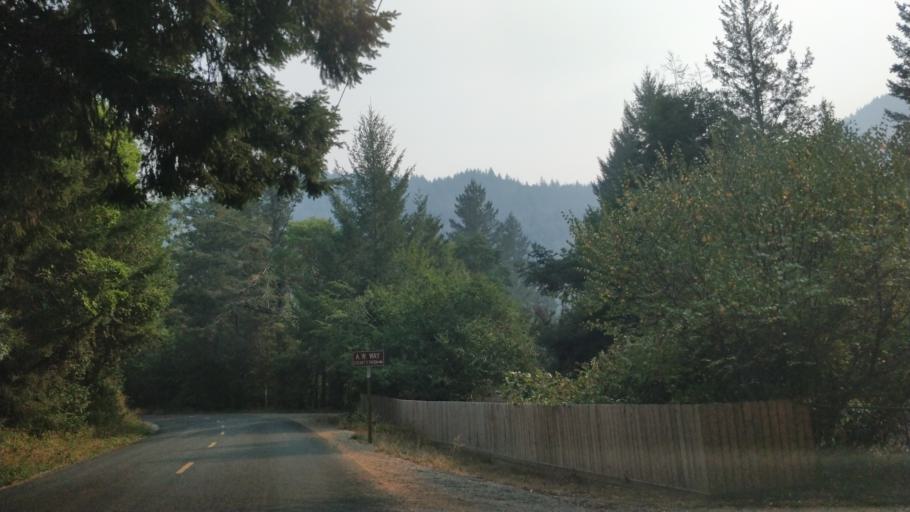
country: US
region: California
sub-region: Humboldt County
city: Rio Dell
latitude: 40.2698
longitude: -124.2300
